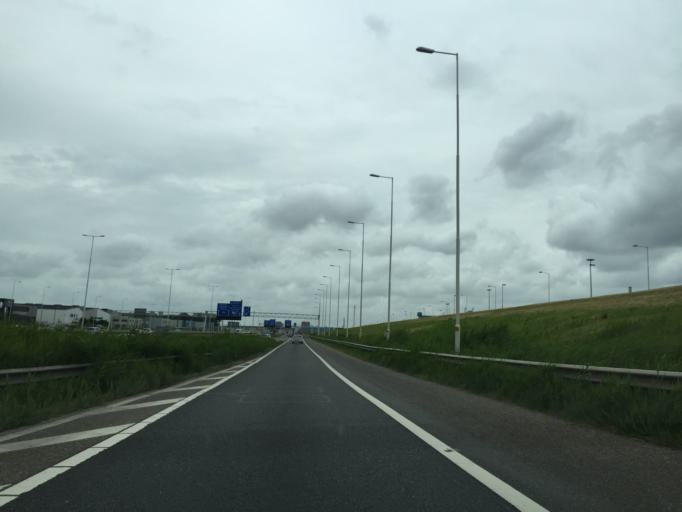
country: NL
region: South Holland
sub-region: Gemeente Albrandswaard
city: Rhoon
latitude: 51.8720
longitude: 4.4244
